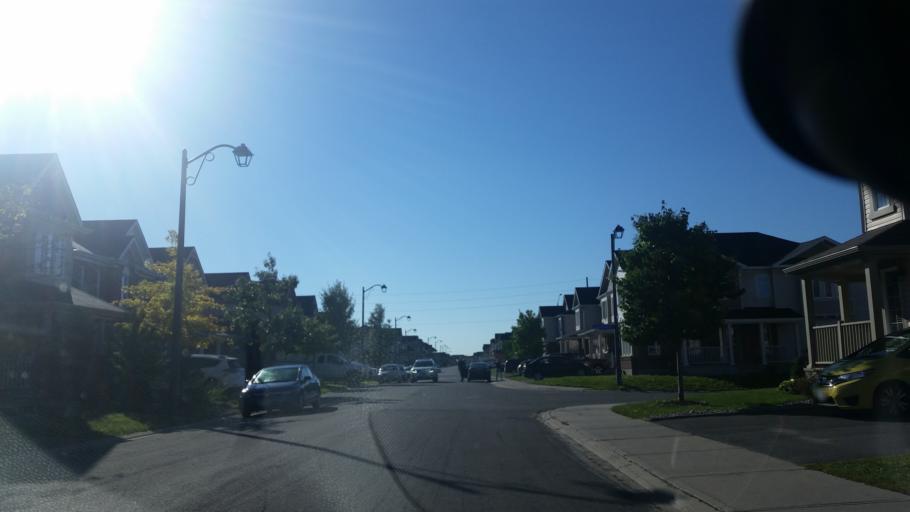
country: CA
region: Ontario
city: Bells Corners
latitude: 45.2510
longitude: -75.7443
